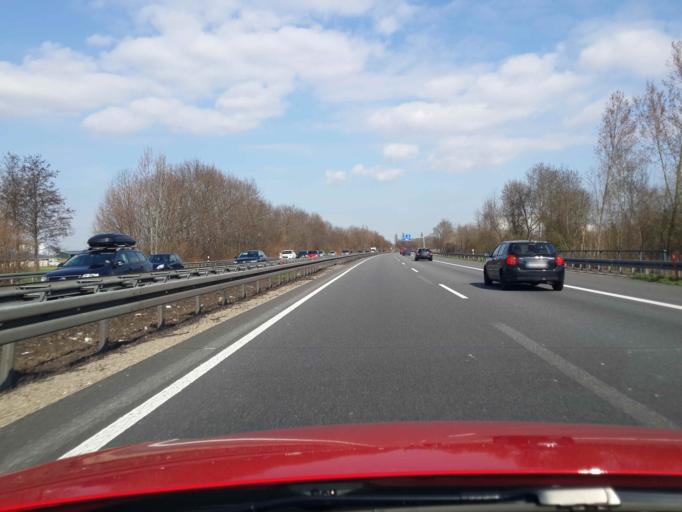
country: DE
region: Hesse
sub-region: Regierungsbezirk Darmstadt
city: Heppenheim an der Bergstrasse
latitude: 49.6341
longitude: 8.6111
